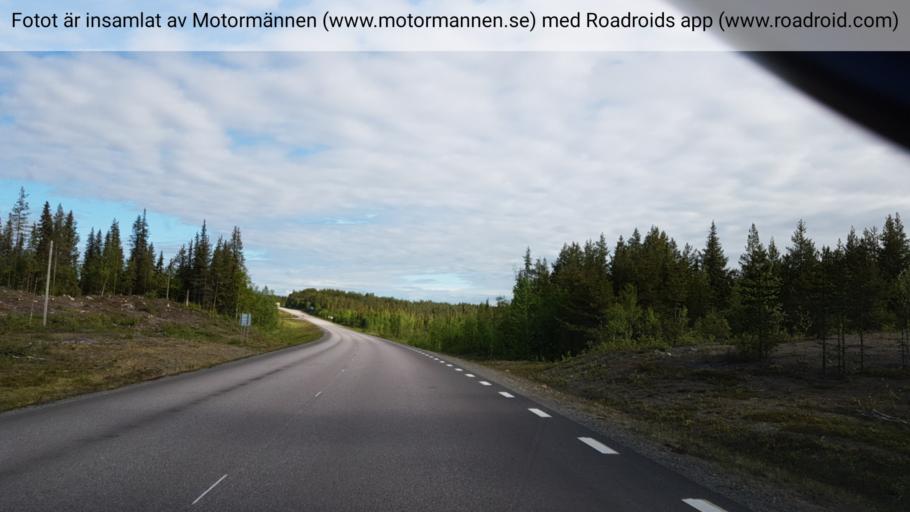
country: SE
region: Norrbotten
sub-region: Gallivare Kommun
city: Malmberget
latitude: 67.4756
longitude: 21.1284
